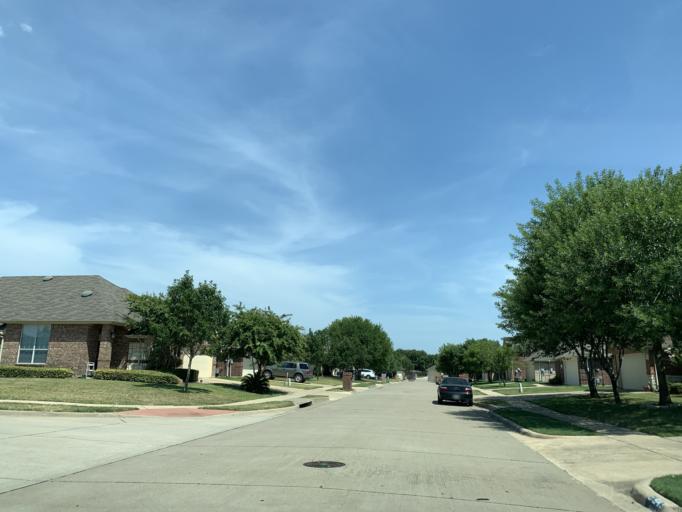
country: US
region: Texas
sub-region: Dallas County
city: Cedar Hill
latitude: 32.6439
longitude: -97.0180
